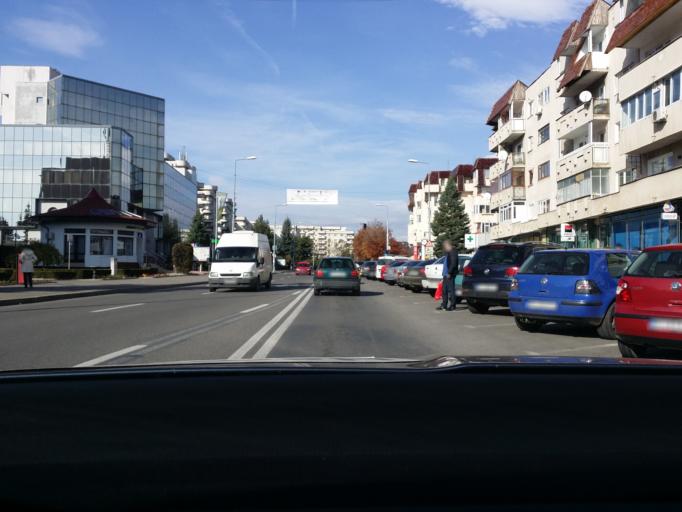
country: RO
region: Prahova
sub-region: Municipiul Campina
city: Campina
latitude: 45.1238
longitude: 25.7352
